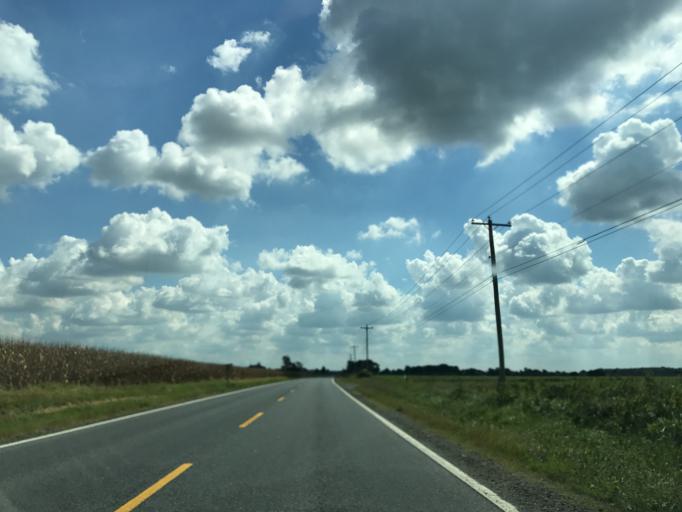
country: US
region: Maryland
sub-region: Queen Anne's County
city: Centreville
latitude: 39.0186
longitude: -76.0061
